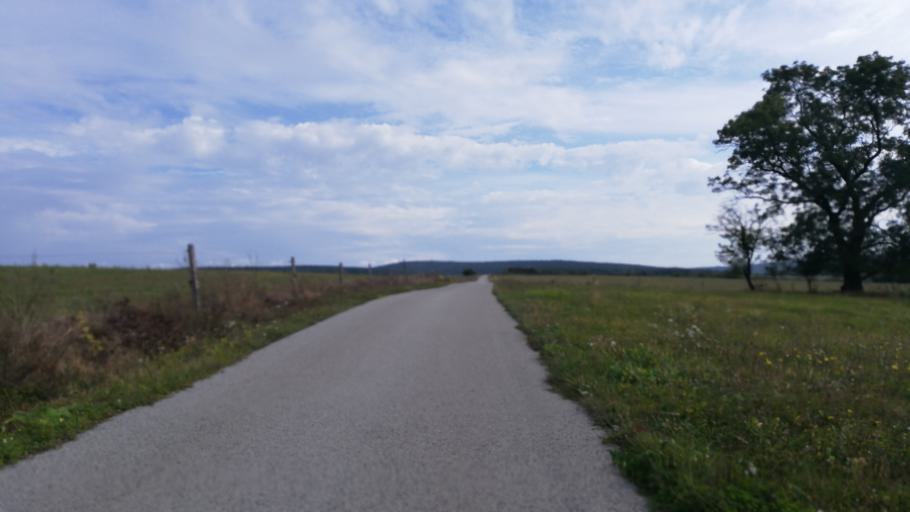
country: CZ
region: South Moravian
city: Sudomerice
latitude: 48.8407
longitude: 17.2878
